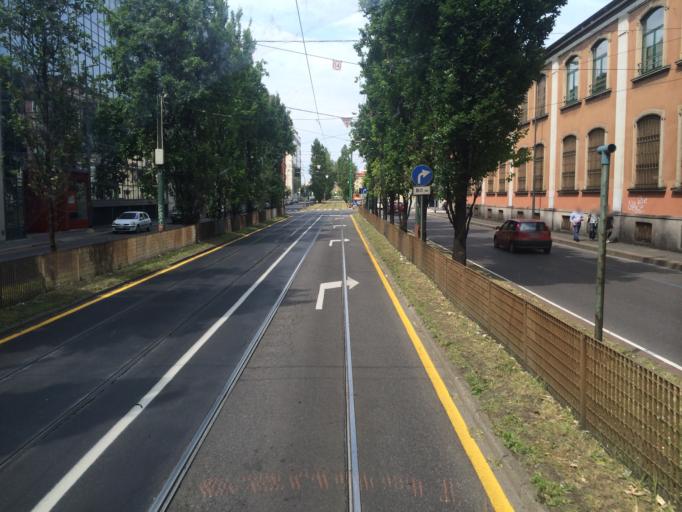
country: IT
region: Lombardy
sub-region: Citta metropolitana di Milano
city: Milano
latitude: 45.4956
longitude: 9.1787
